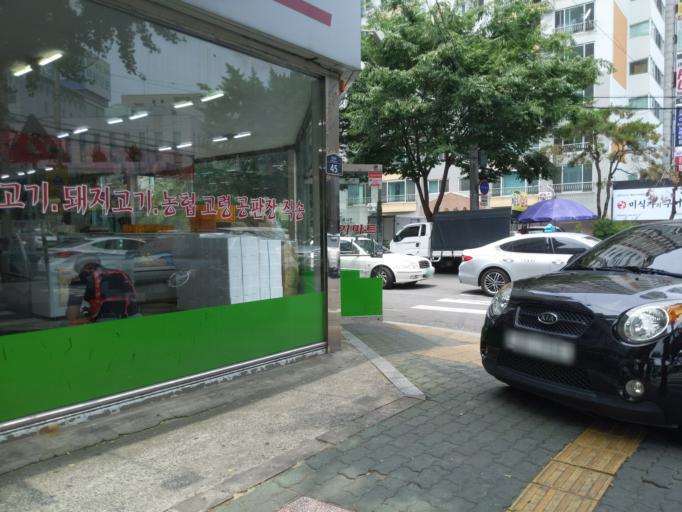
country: KR
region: Daegu
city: Hwawon
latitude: 35.8128
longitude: 128.5247
